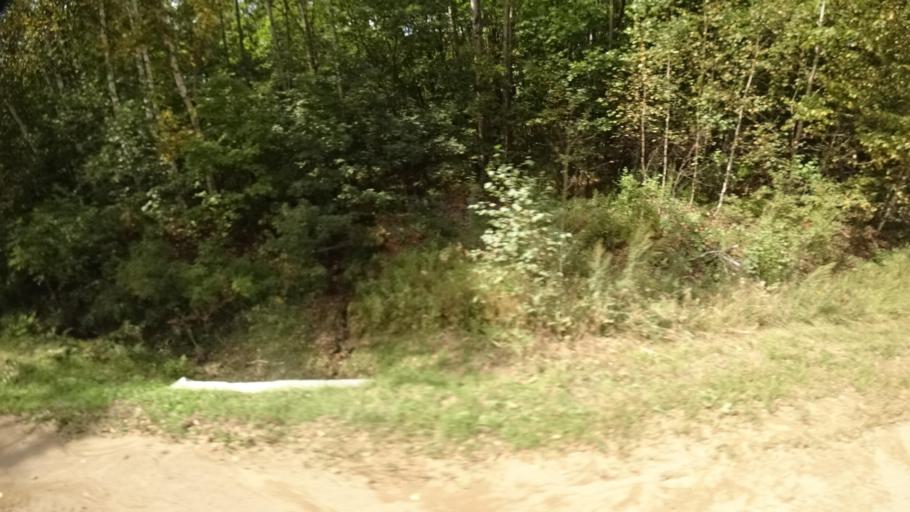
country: RU
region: Primorskiy
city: Yakovlevka
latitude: 44.6689
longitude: 133.6108
